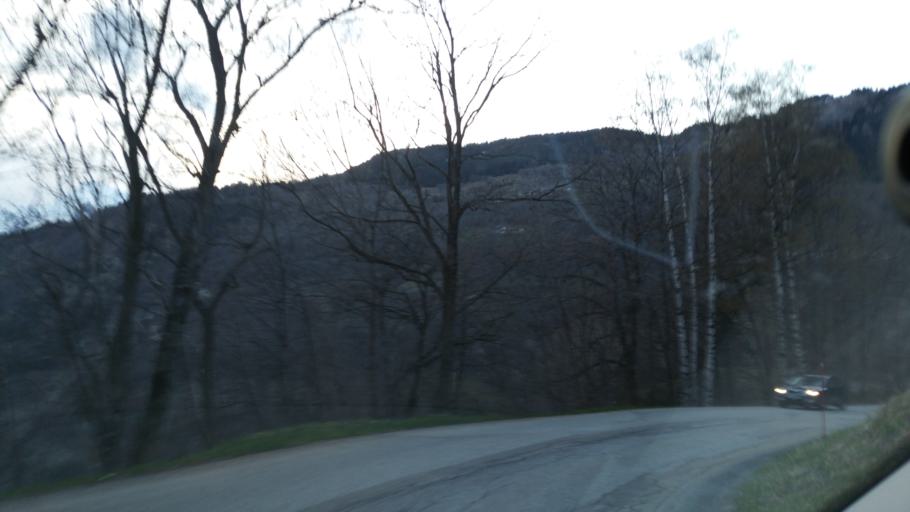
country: FR
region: Rhone-Alpes
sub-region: Departement de la Savoie
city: La Chambre
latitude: 45.3847
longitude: 6.3305
